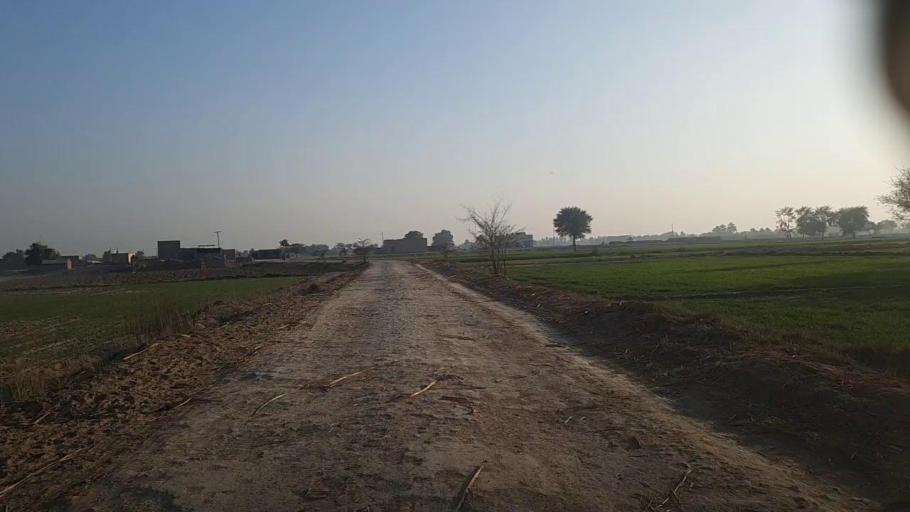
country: PK
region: Sindh
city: Khairpur
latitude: 28.0664
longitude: 69.7520
